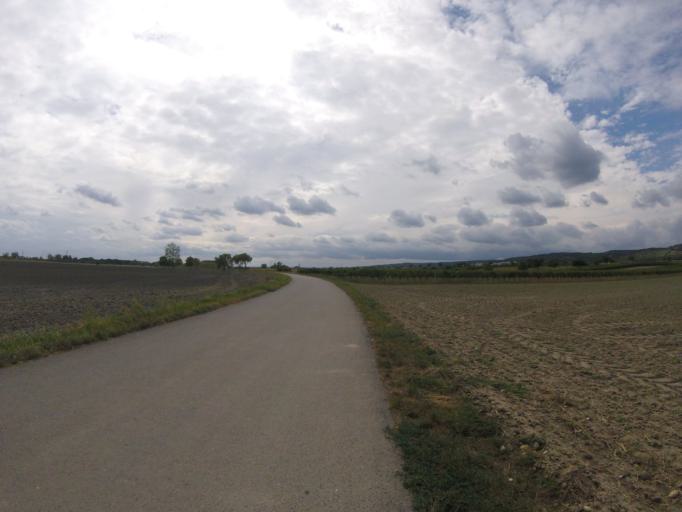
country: AT
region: Burgenland
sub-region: Eisenstadt-Umgebung
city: Breitenbrunn
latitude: 47.9244
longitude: 16.7156
